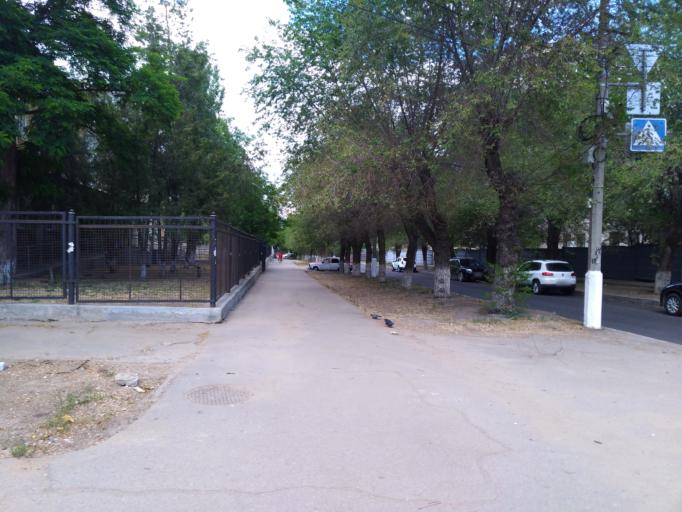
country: RU
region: Volgograd
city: Volgograd
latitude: 48.7183
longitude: 44.5343
